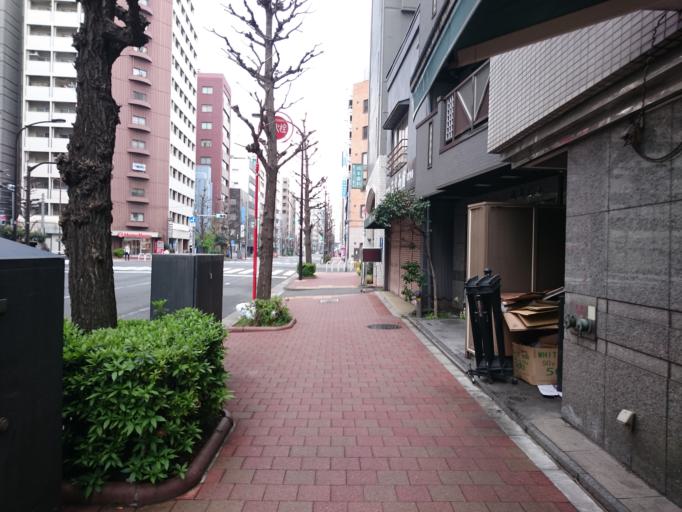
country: JP
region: Tokyo
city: Tokyo
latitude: 35.6922
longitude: 139.7775
